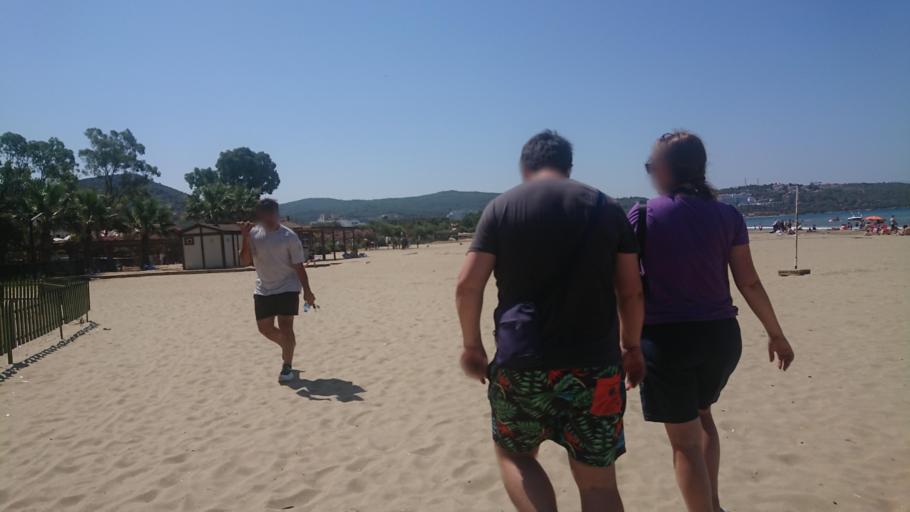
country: TR
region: Aydin
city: Kusadasi
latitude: 37.9374
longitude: 27.2758
